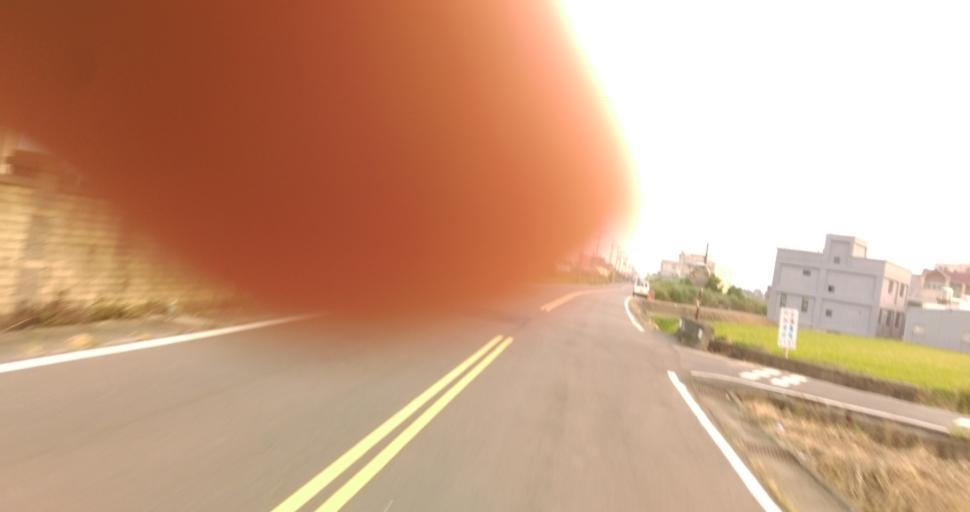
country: TW
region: Taiwan
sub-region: Hsinchu
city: Zhubei
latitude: 24.8707
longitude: 120.9580
